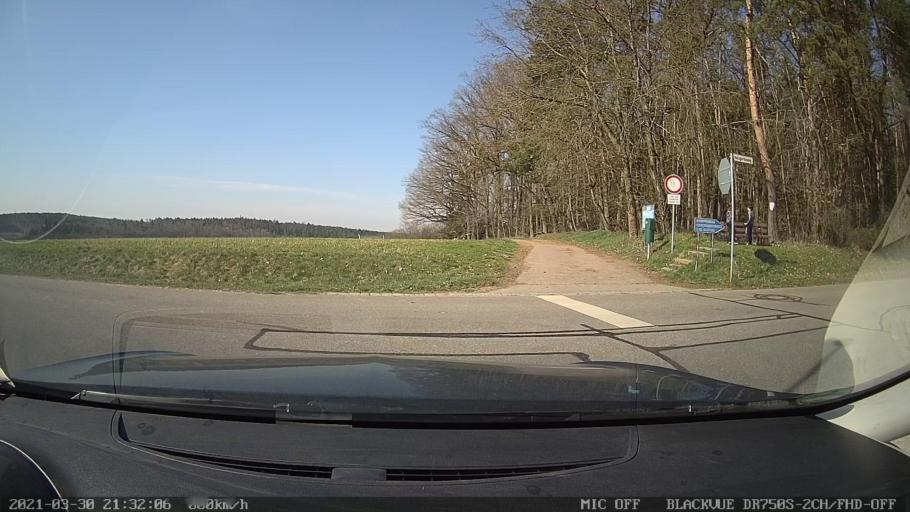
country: DE
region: Bavaria
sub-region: Upper Palatinate
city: Zeitlarn
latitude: 49.0958
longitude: 12.1016
